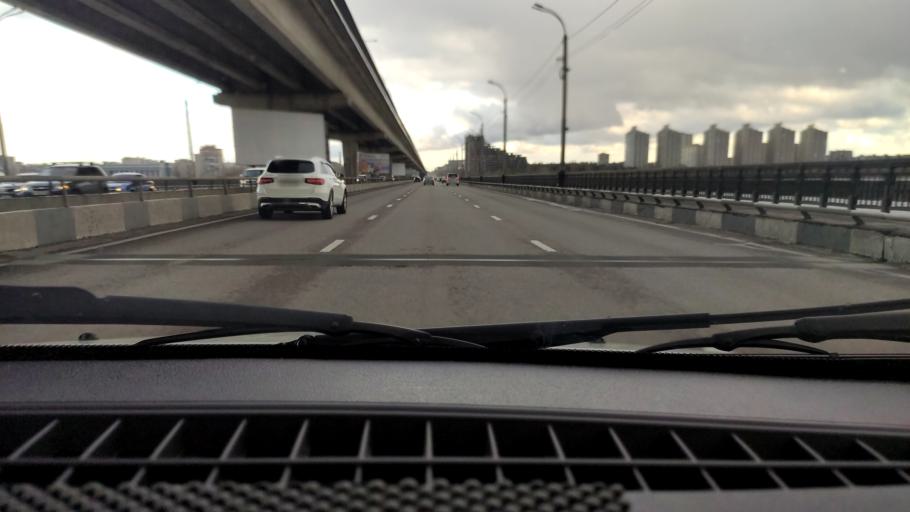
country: RU
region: Voronezj
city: Voronezh
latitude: 51.6945
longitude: 39.2510
